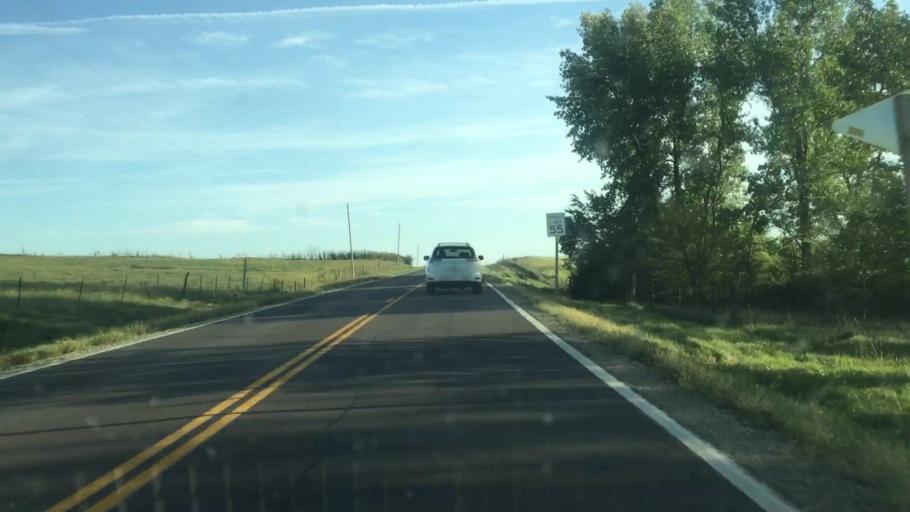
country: US
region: Kansas
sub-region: Brown County
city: Horton
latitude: 39.5841
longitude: -95.5270
